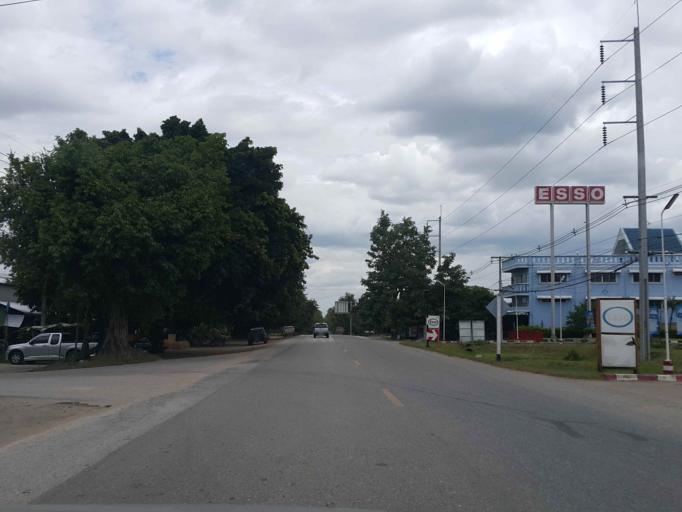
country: TH
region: Chiang Mai
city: Doi Lo
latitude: 18.4273
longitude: 98.8638
